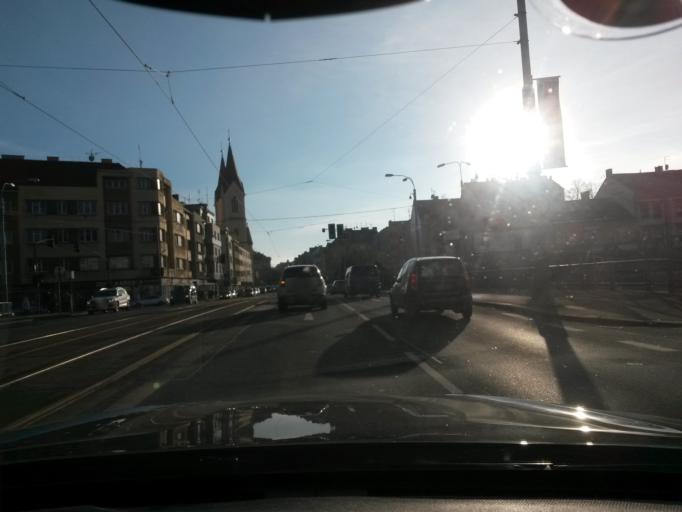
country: CZ
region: Plzensky
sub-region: Okres Plzen-Mesto
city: Pilsen
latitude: 49.7404
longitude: 13.3712
